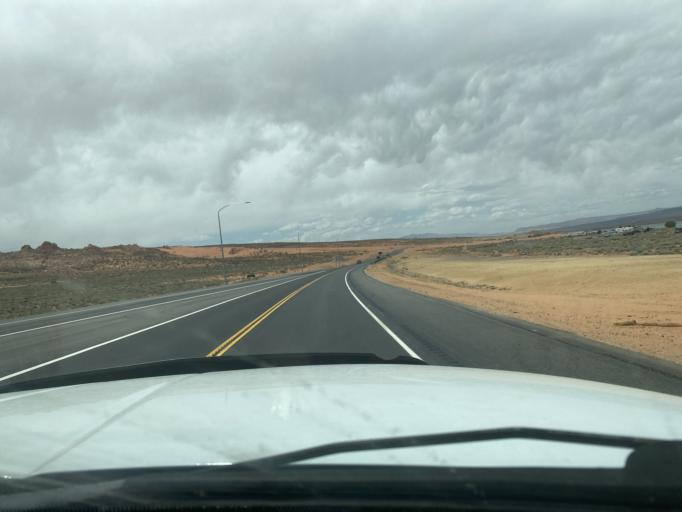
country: US
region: Utah
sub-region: Washington County
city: Hurricane
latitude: 37.0981
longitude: -113.3646
